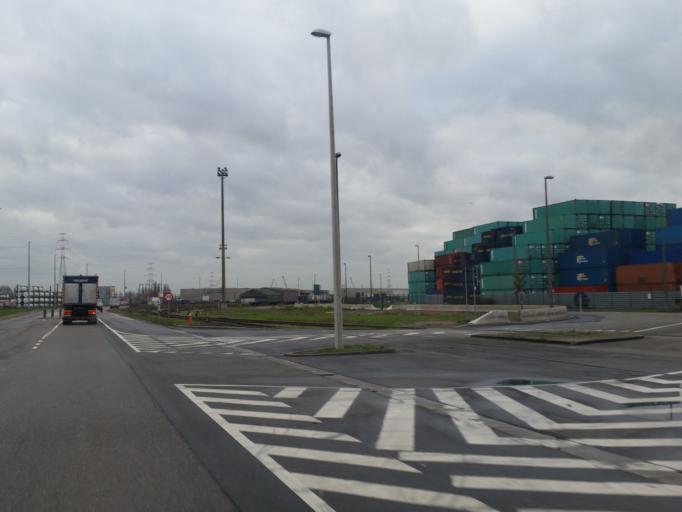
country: BE
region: Flanders
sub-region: Provincie Antwerpen
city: Stabroek
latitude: 51.2783
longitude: 4.3851
